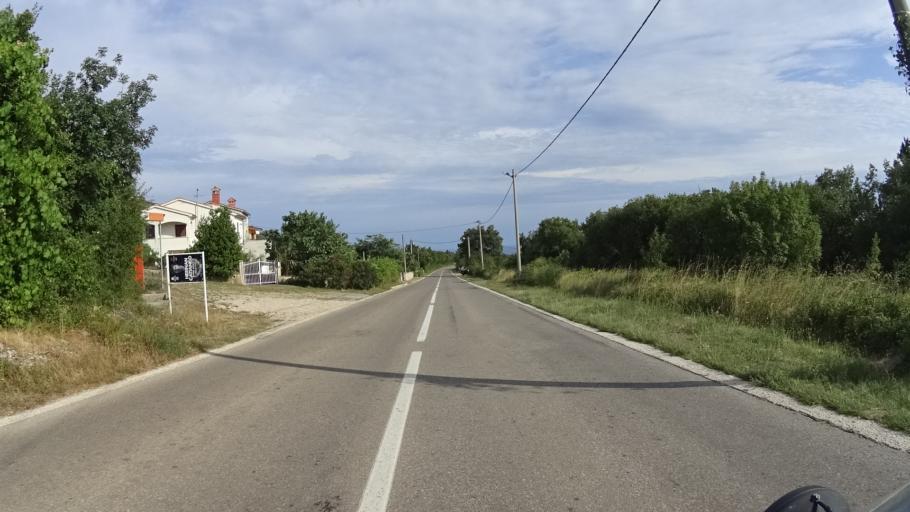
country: HR
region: Istarska
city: Rasa
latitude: 45.0039
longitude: 14.0994
